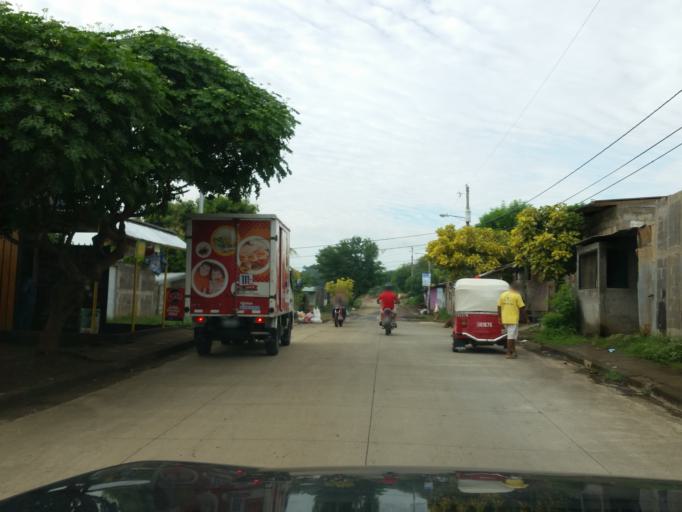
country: NI
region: Managua
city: Managua
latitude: 12.1029
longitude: -86.2273
